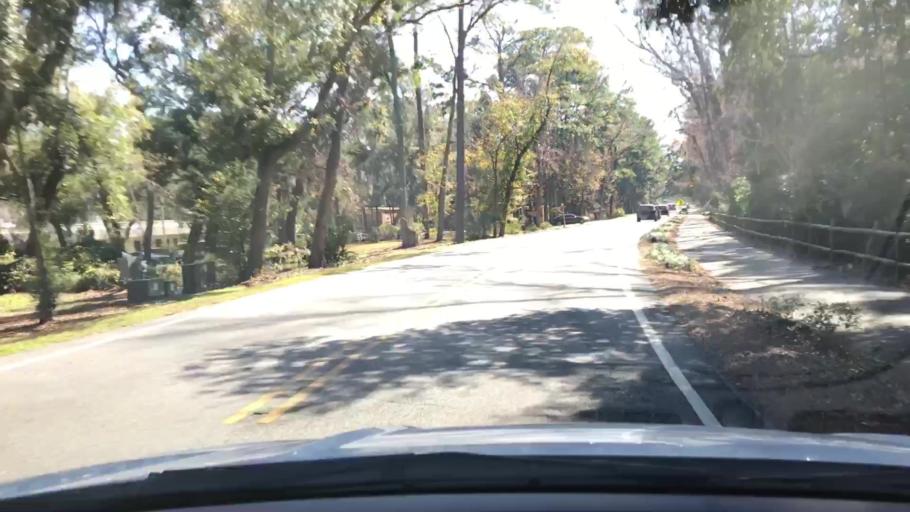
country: US
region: South Carolina
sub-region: Beaufort County
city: Hilton Head Island
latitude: 32.2221
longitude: -80.7057
